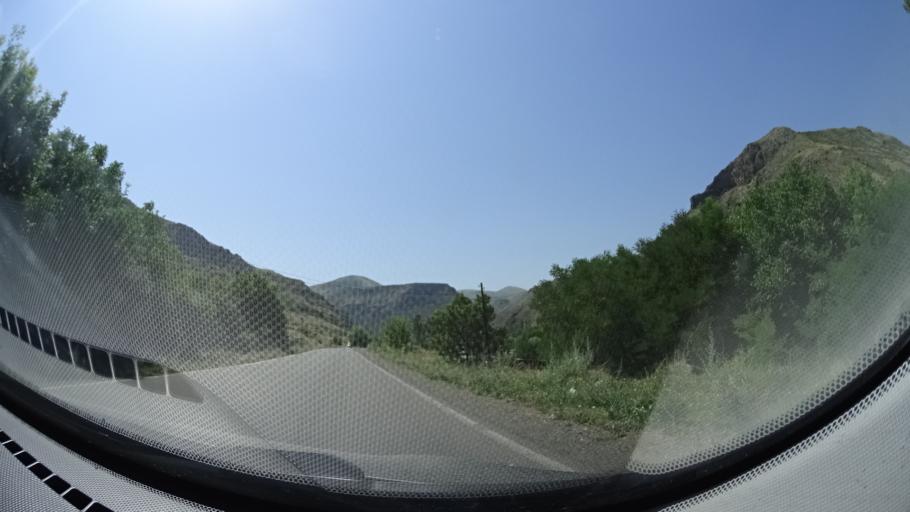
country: GE
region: Samtskhe-Javakheti
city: Aspindza
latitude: 41.4959
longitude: 43.2656
